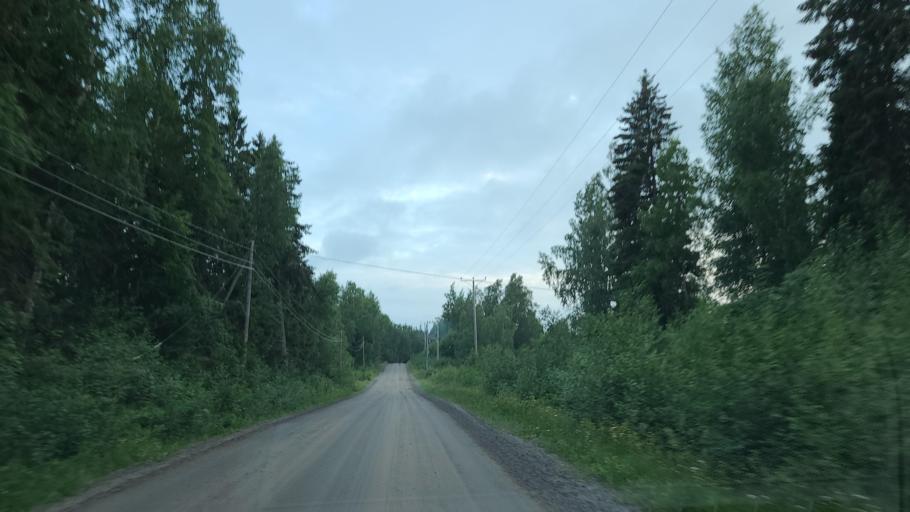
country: FI
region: Ostrobothnia
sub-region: Vaasa
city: Replot
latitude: 63.2967
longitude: 21.1215
